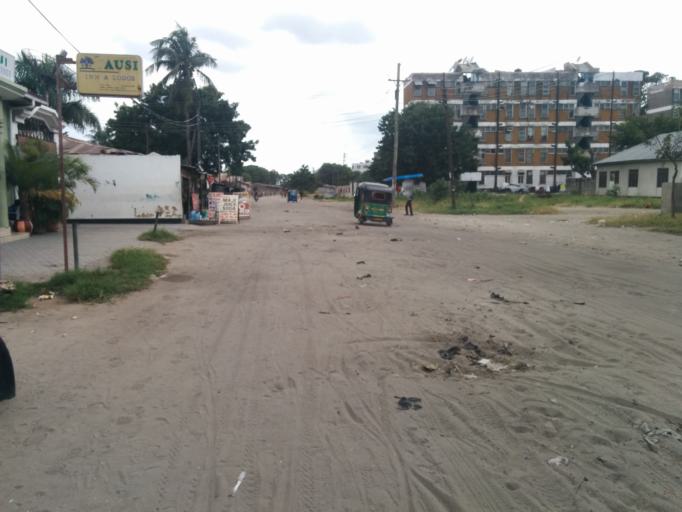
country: TZ
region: Dar es Salaam
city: Dar es Salaam
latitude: -6.8647
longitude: 39.2555
